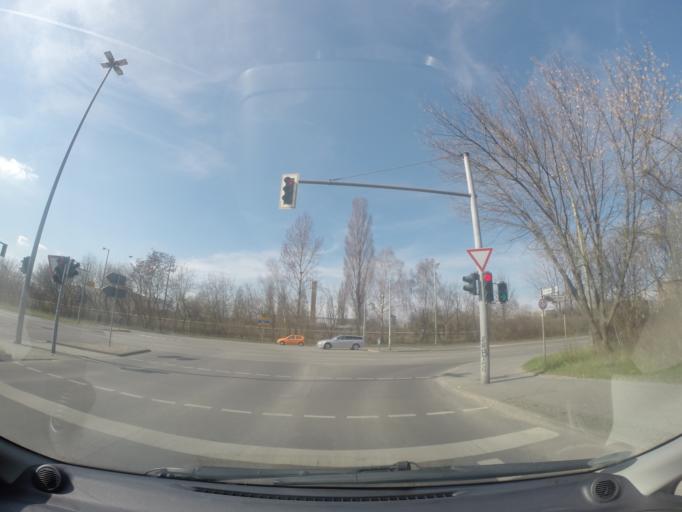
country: DE
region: Berlin
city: Falkenberg
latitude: 52.5544
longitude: 13.5519
